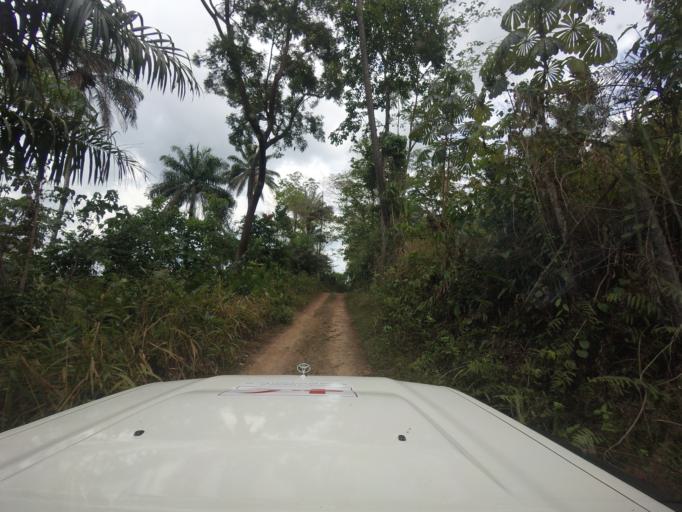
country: LR
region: Lofa
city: Voinjama
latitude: 8.3928
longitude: -9.6266
